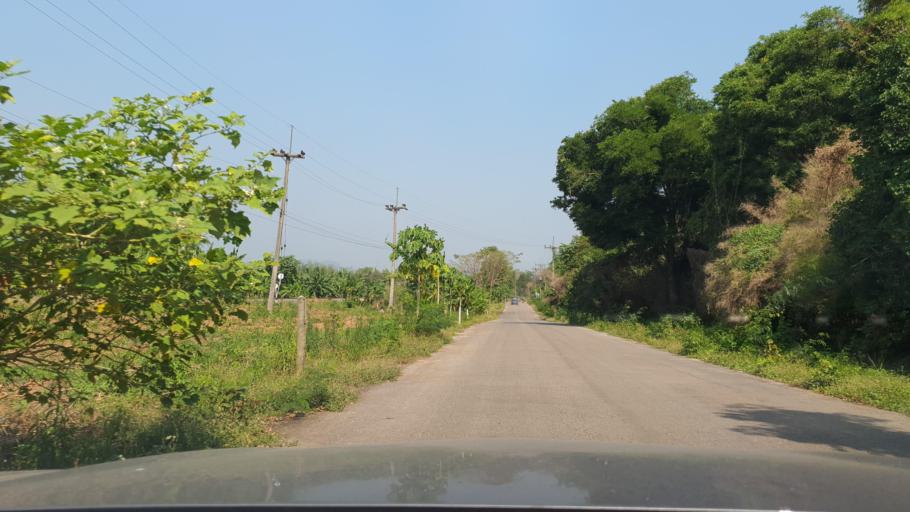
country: TH
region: Kanchanaburi
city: Sai Yok
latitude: 14.0968
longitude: 99.1744
